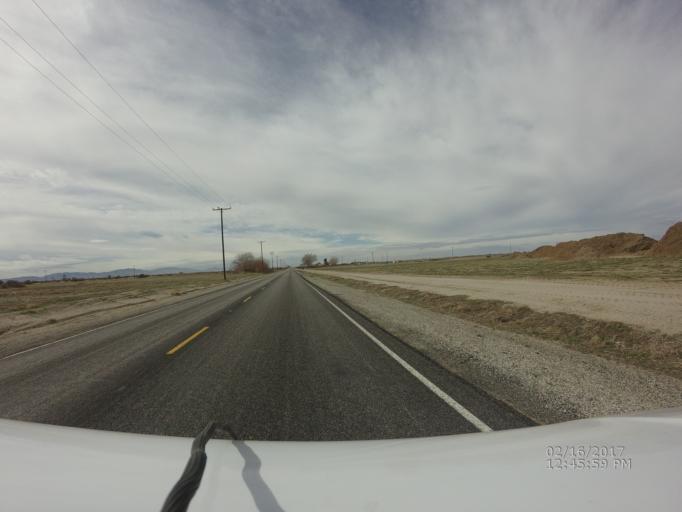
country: US
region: California
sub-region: Los Angeles County
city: Lake Los Angeles
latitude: 34.6755
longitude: -117.9497
